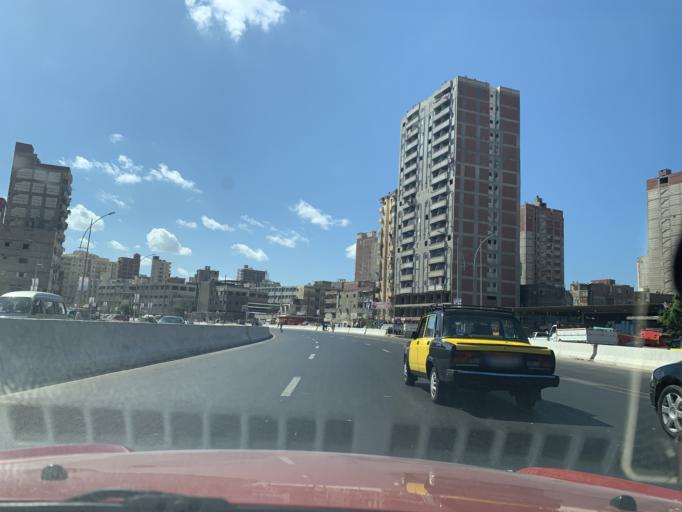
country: EG
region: Alexandria
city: Alexandria
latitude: 31.2019
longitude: 29.9377
